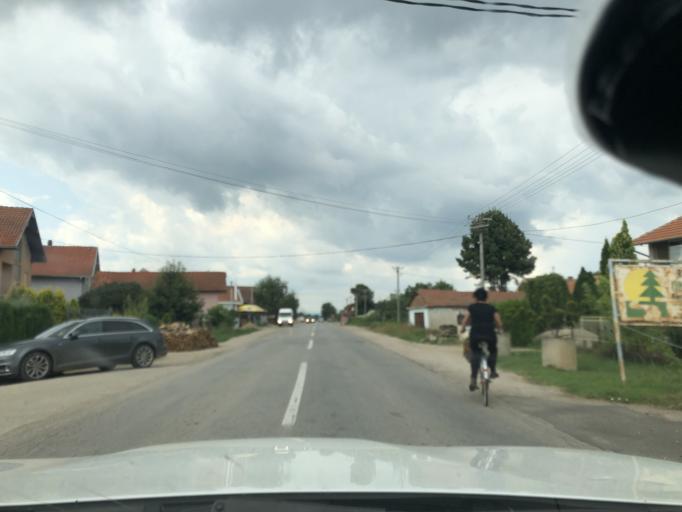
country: RS
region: Central Serbia
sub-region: Jablanicki Okrug
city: Leskovac
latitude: 42.9704
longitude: 21.8802
